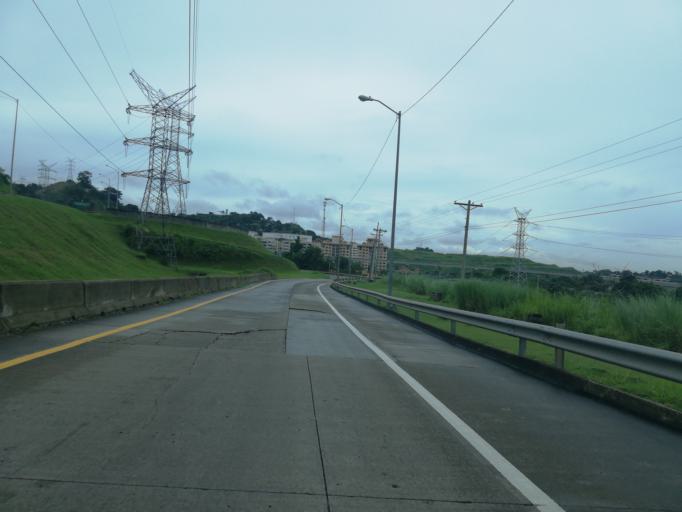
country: PA
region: Panama
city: Las Cumbres
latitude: 9.0566
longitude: -79.5132
